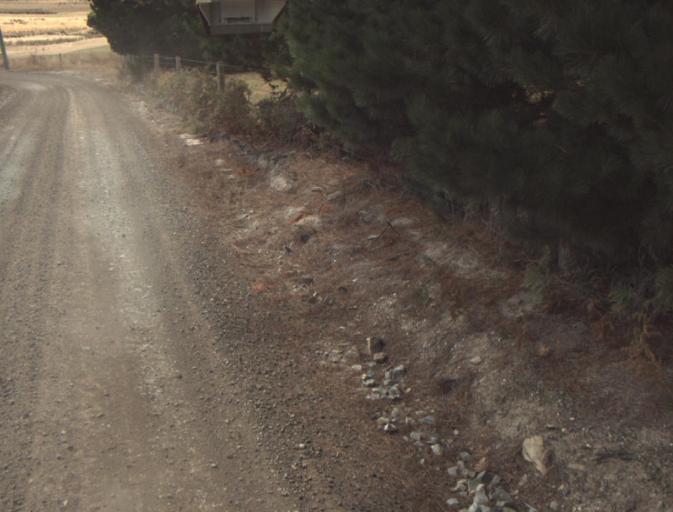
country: AU
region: Tasmania
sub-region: Launceston
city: Mayfield
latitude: -41.1985
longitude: 147.1687
